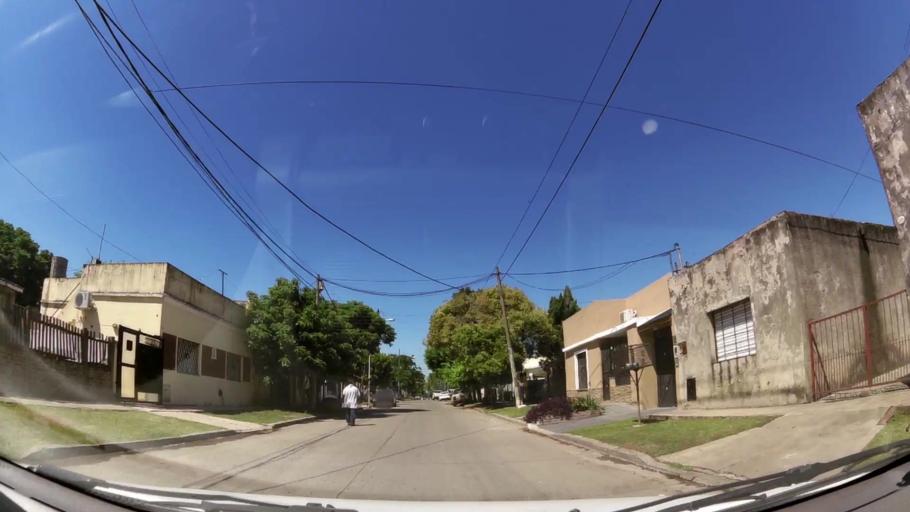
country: AR
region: Buenos Aires
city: Ituzaingo
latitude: -34.6833
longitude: -58.6569
